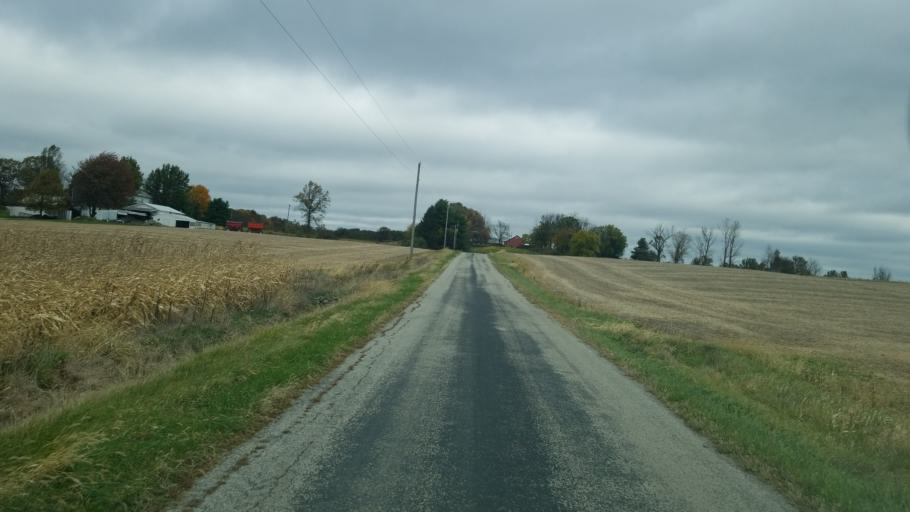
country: US
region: Ohio
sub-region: Huron County
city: Willard
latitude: 40.9433
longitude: -82.8116
